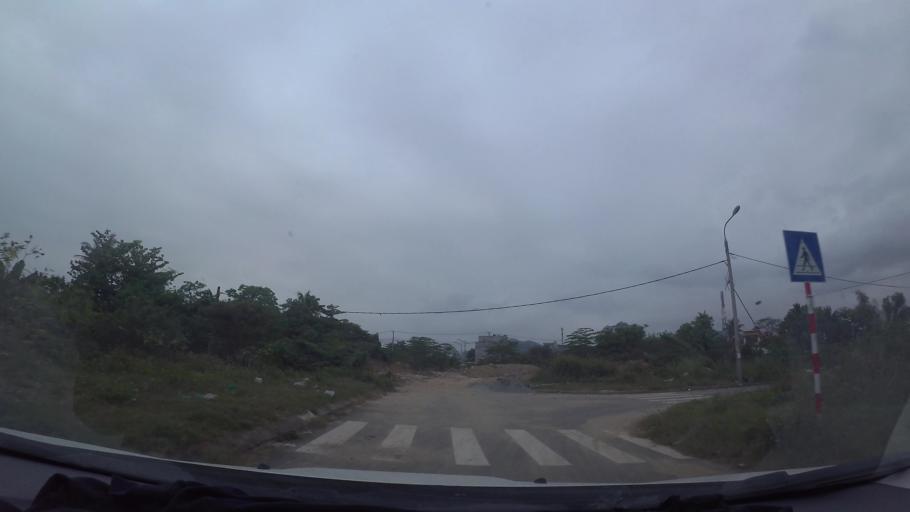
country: VN
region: Da Nang
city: Lien Chieu
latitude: 16.0768
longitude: 108.1574
